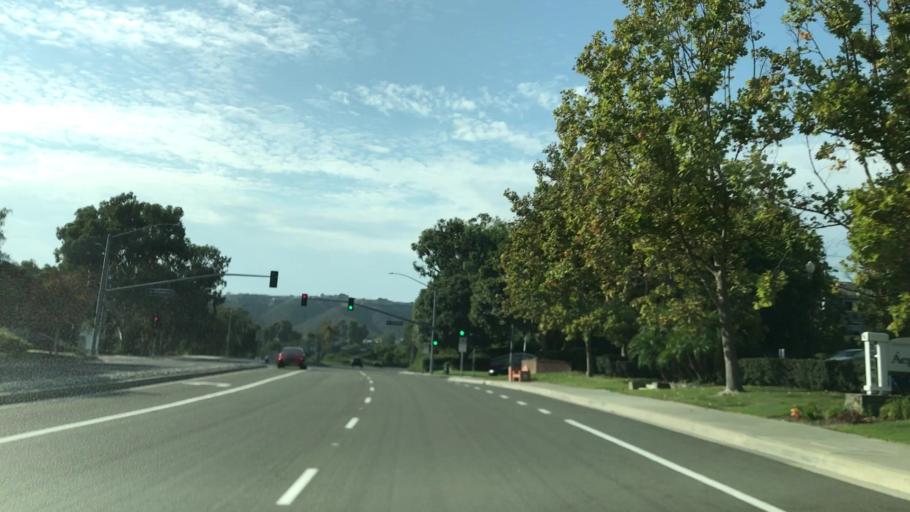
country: US
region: California
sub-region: Orange County
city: Laguna Niguel
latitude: 33.4956
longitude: -117.7100
